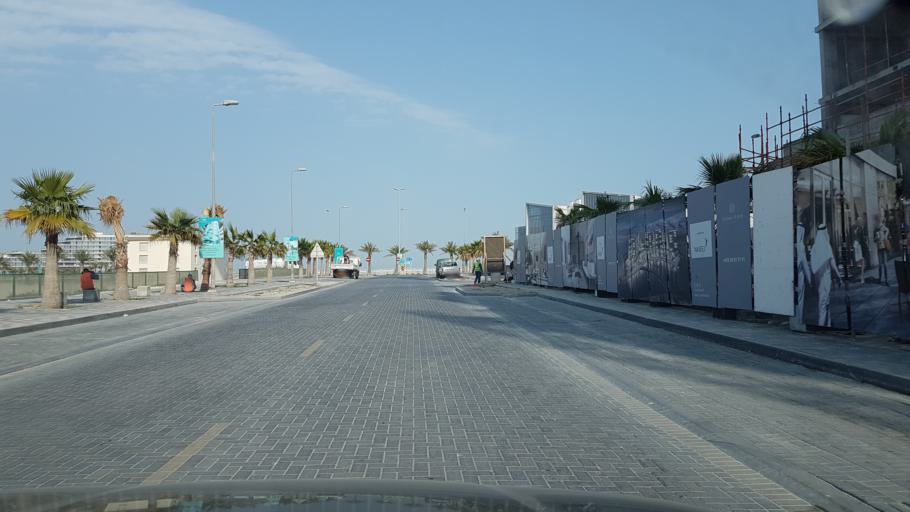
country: BH
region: Muharraq
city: Al Hadd
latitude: 26.2703
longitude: 50.6685
